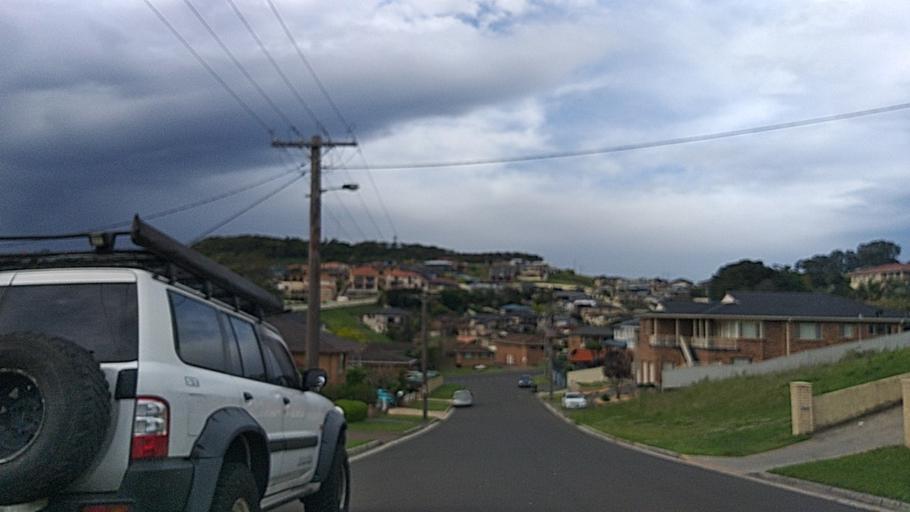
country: AU
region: New South Wales
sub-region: Wollongong
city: Berkeley
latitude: -34.4817
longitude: 150.8613
